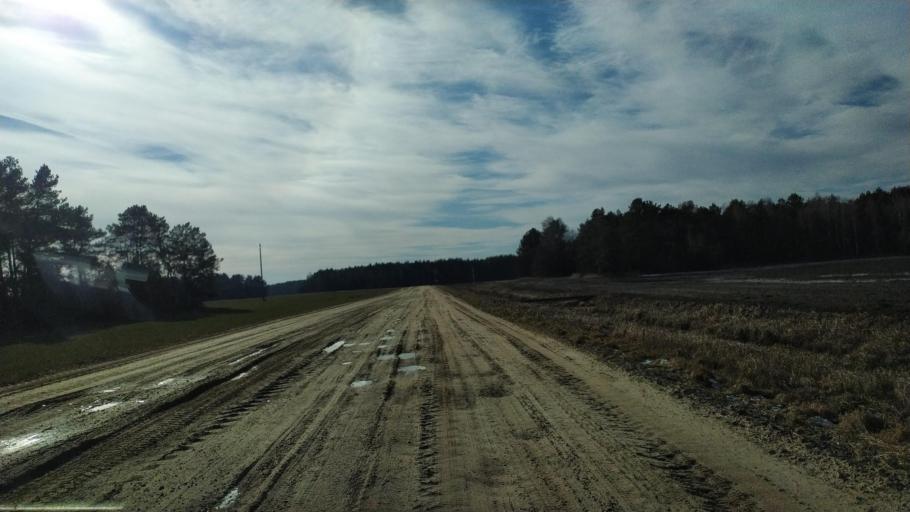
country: BY
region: Brest
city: Pruzhany
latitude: 52.5734
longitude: 24.3008
